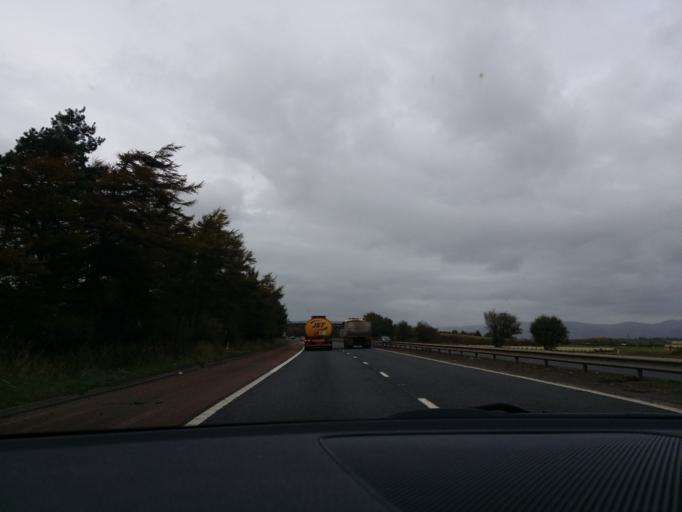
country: GB
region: Scotland
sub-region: Falkirk
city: Airth
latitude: 56.0358
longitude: -3.7688
